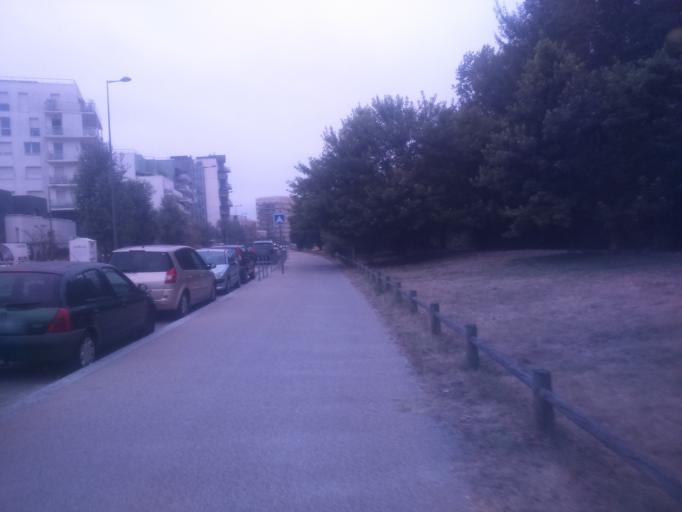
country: FR
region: Aquitaine
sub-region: Departement de la Gironde
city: Le Bouscat
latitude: 44.8813
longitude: -0.5729
